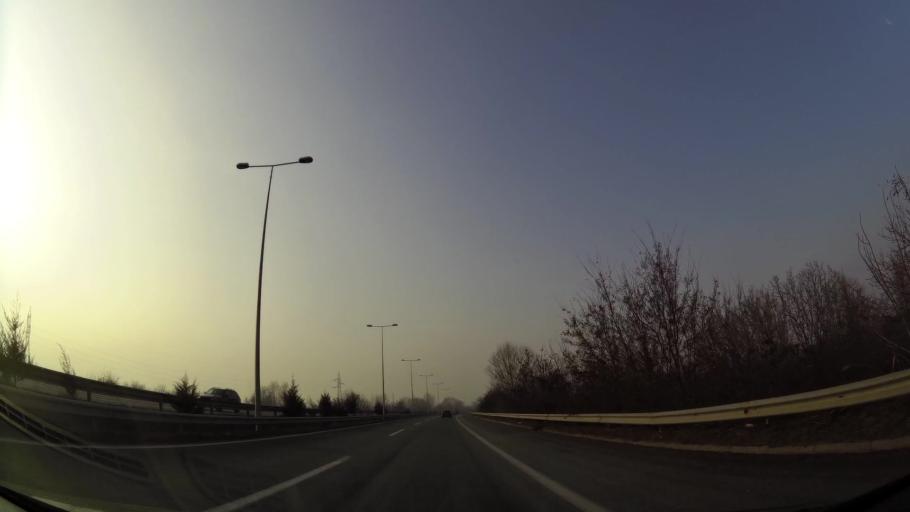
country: MK
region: Ilinden
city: Jurumleri
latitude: 41.9770
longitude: 21.5486
